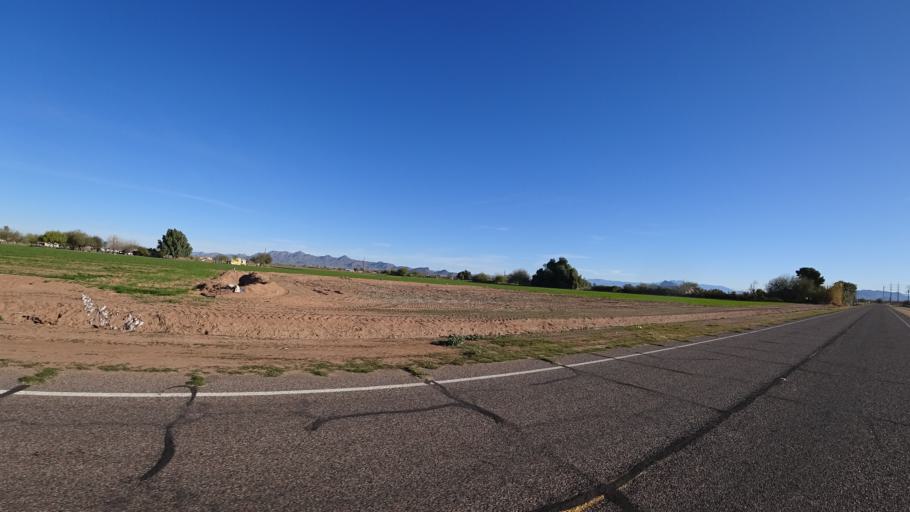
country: US
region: Arizona
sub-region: Maricopa County
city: Mesa
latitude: 33.4806
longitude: -111.8375
